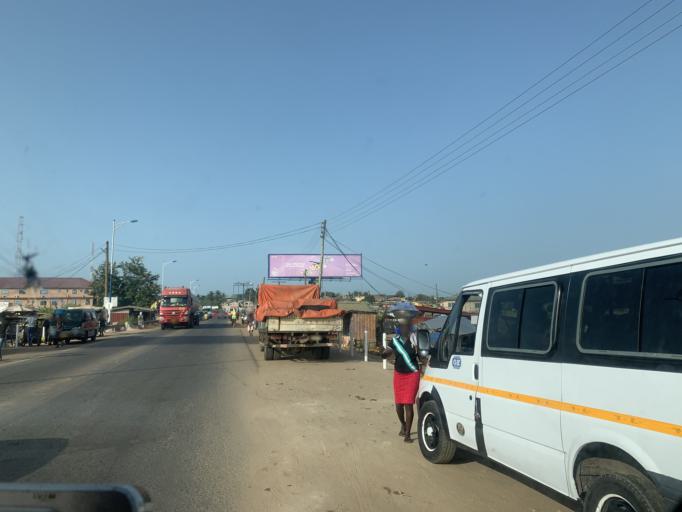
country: GH
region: Central
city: Saltpond
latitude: 5.2667
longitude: -1.0191
